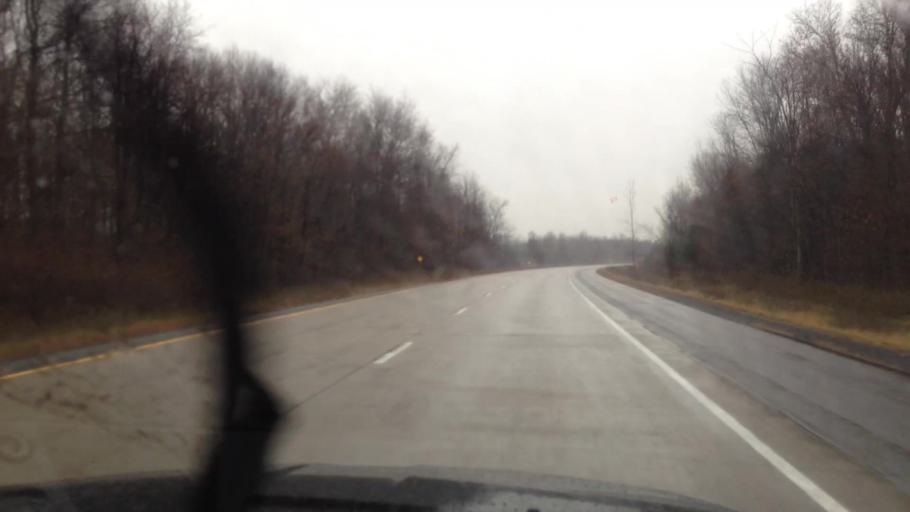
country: CA
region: Ontario
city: Hawkesbury
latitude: 45.4467
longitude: -74.7224
